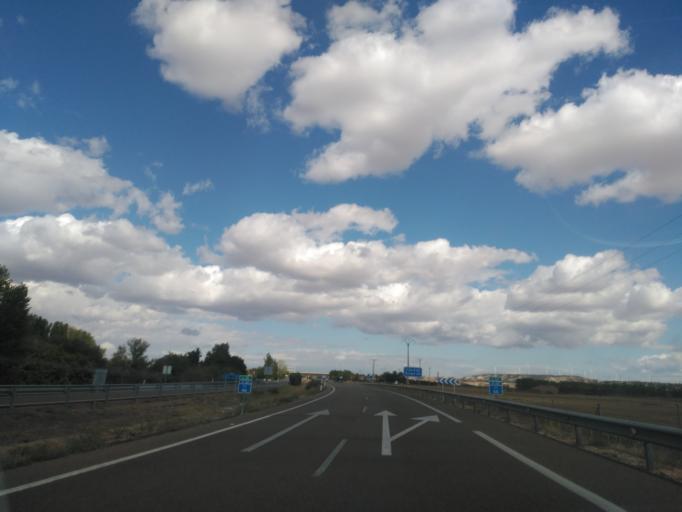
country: ES
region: Castille and Leon
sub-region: Provincia de Palencia
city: Torquemada
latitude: 42.0298
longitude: -4.3041
